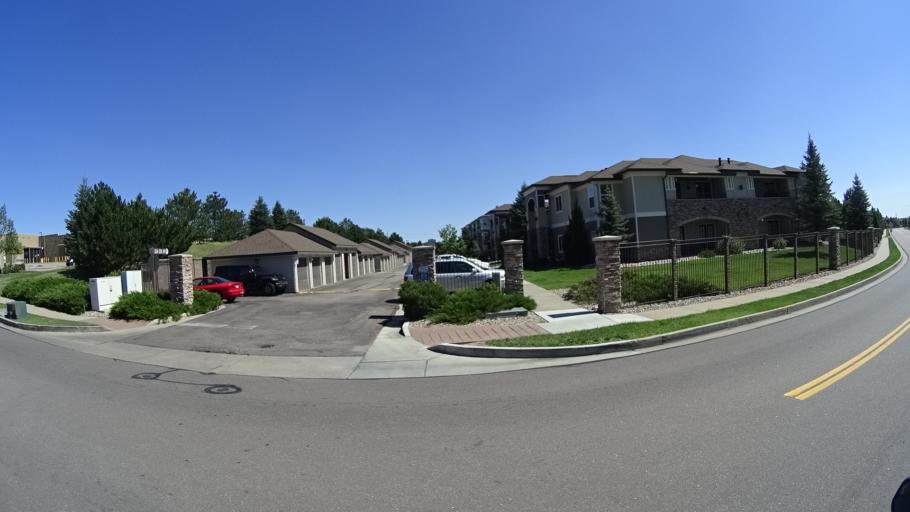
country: US
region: Colorado
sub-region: El Paso County
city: Cimarron Hills
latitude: 38.8533
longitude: -104.7235
